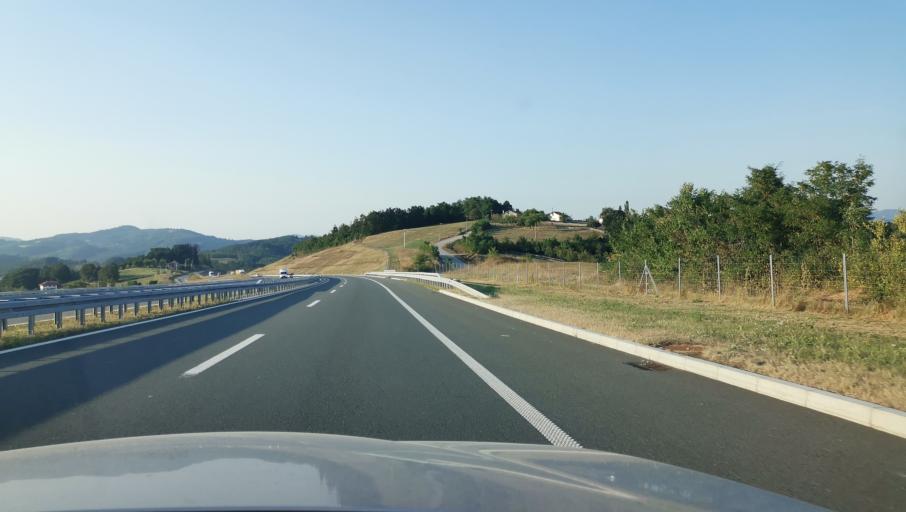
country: RS
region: Central Serbia
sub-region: Moravicki Okrug
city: Gornji Milanovac
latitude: 44.1027
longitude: 20.3847
